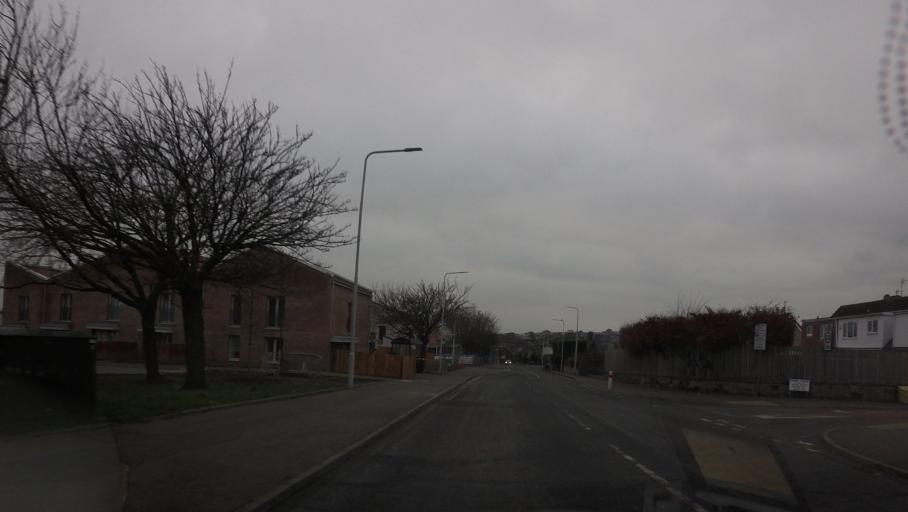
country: GB
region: Scotland
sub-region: Fife
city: Inverkeithing
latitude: 56.0333
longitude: -3.3891
